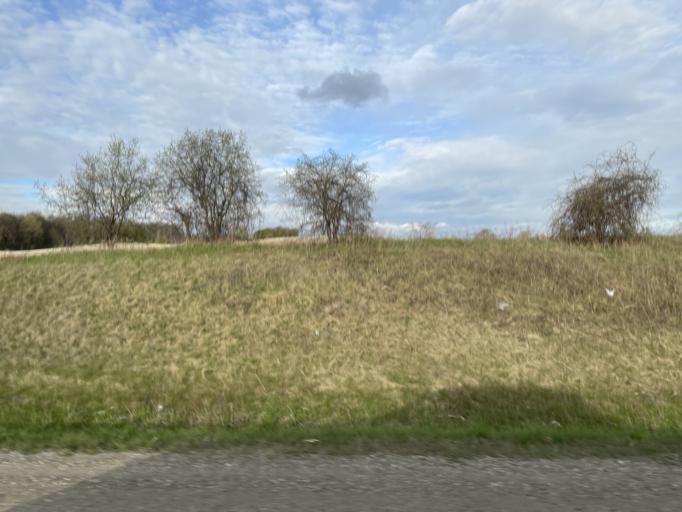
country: CA
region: Ontario
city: Waterloo
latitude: 43.4742
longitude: -80.4023
